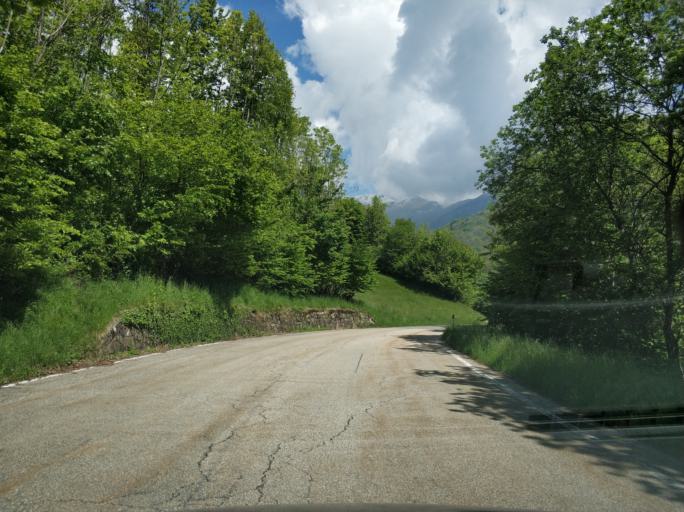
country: IT
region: Piedmont
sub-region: Provincia di Torino
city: Coassolo
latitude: 45.3115
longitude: 7.4706
